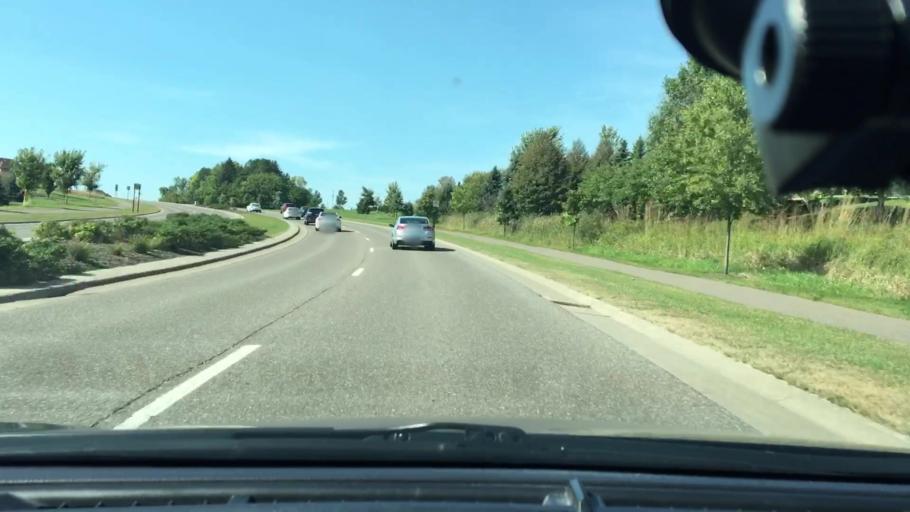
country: US
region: Minnesota
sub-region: Hennepin County
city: Maple Grove
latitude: 45.0846
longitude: -93.4943
